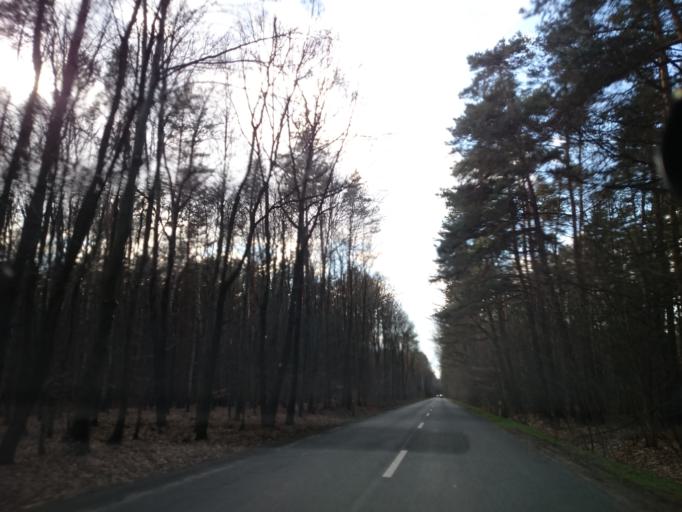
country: PL
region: Opole Voivodeship
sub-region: Powiat opolski
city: Niemodlin
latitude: 50.6240
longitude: 17.5617
